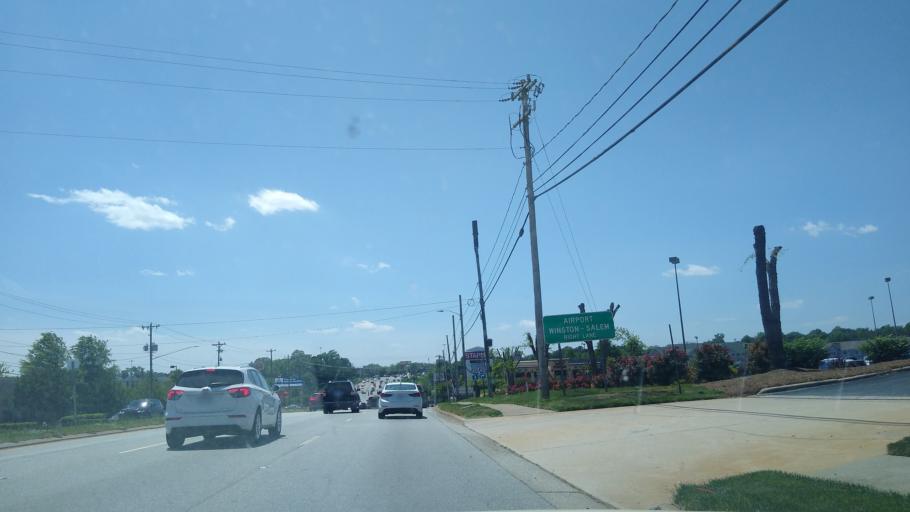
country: US
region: North Carolina
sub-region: Guilford County
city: Jamestown
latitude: 36.0586
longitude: -79.8866
